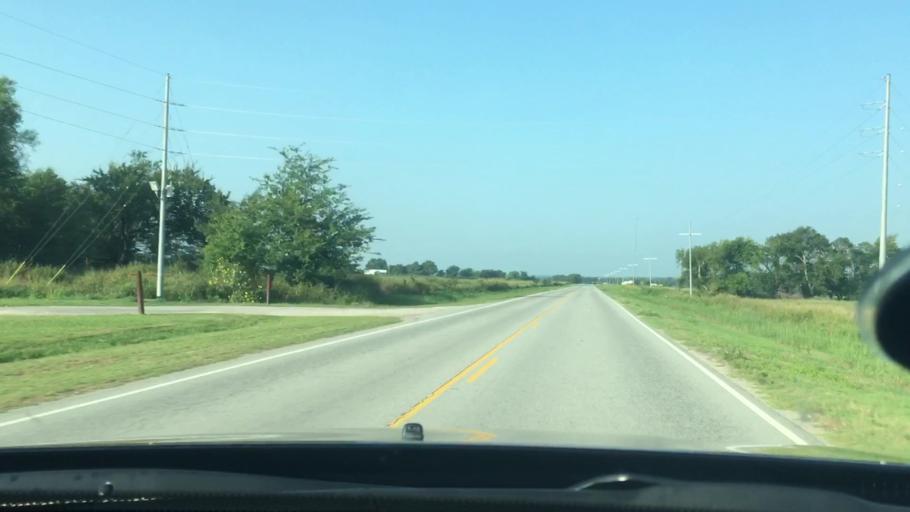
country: US
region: Oklahoma
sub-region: Coal County
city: Coalgate
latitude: 34.4968
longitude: -96.4125
